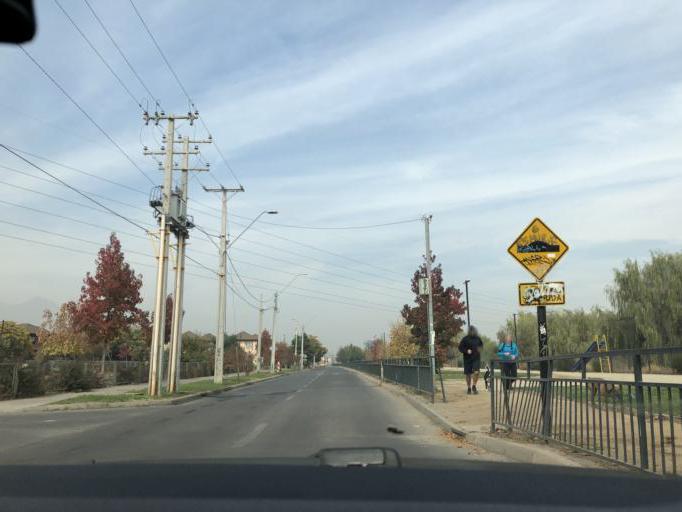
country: CL
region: Santiago Metropolitan
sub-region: Provincia de Cordillera
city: Puente Alto
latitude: -33.5565
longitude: -70.5529
